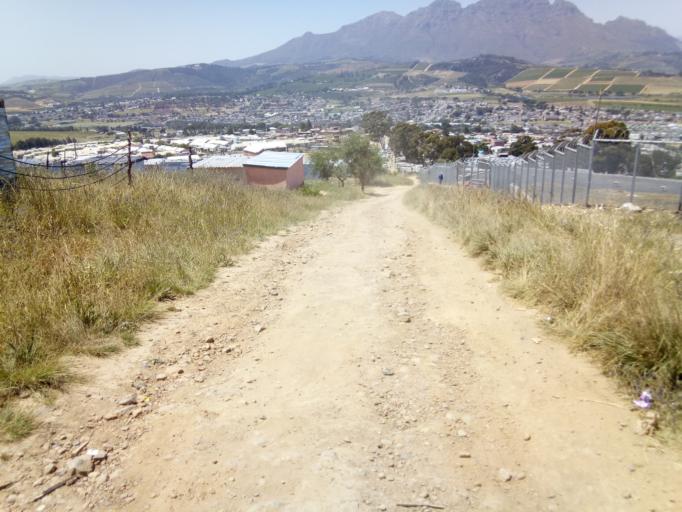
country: ZA
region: Western Cape
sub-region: Cape Winelands District Municipality
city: Stellenbosch
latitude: -33.9247
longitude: 18.8397
